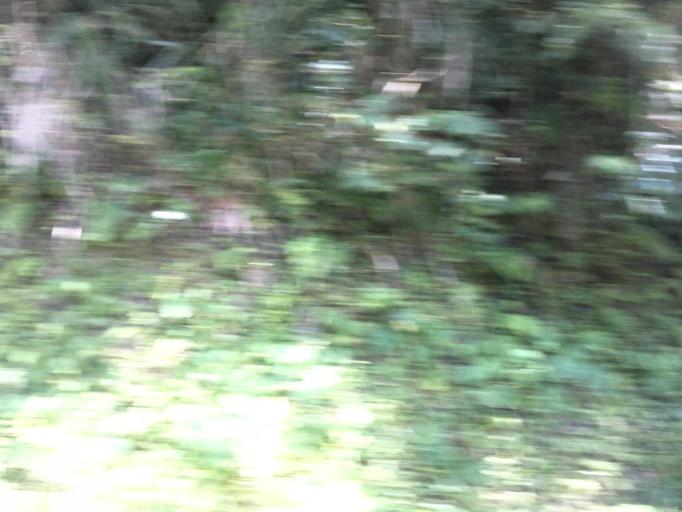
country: TW
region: Taiwan
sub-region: Yilan
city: Yilan
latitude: 24.5324
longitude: 121.5207
